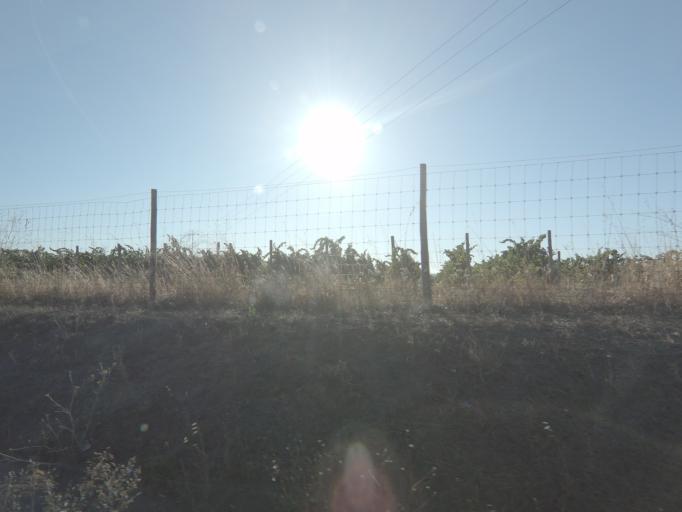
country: PT
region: Setubal
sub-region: Palmela
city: Quinta do Anjo
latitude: 38.5443
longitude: -8.9845
